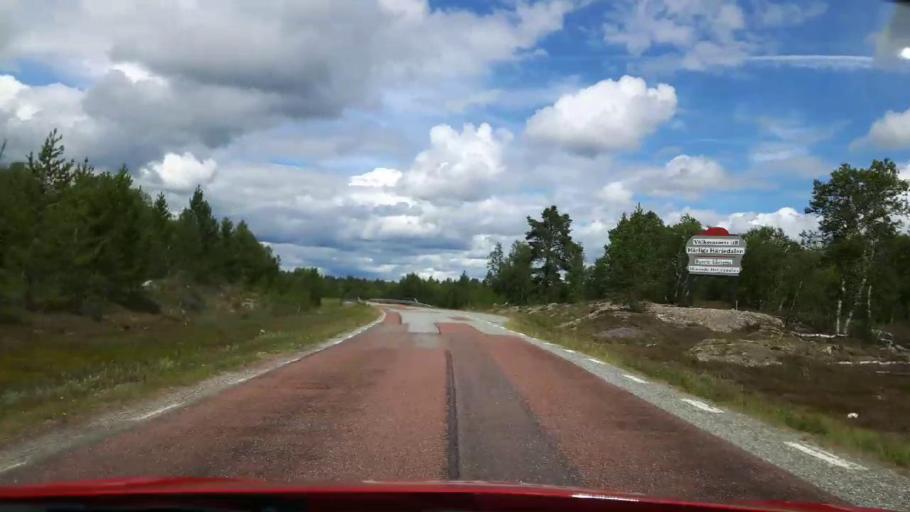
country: NO
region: Hedmark
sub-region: Trysil
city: Innbygda
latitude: 62.1027
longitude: 12.9831
